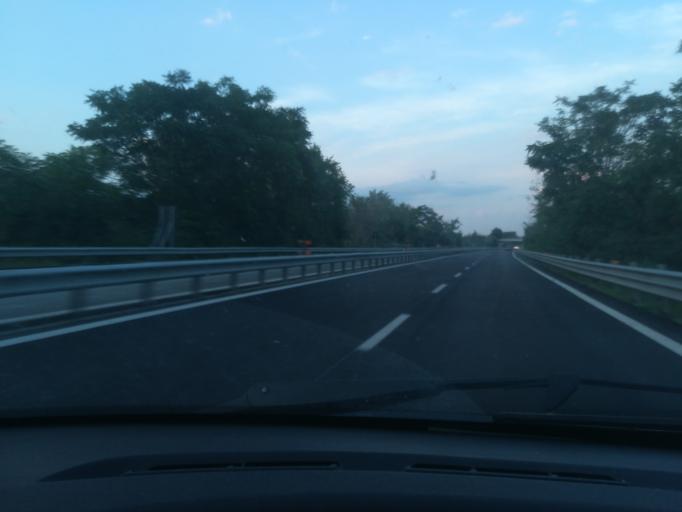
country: IT
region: The Marches
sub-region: Provincia di Macerata
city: Sforzacosta
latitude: 43.2540
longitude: 13.4463
